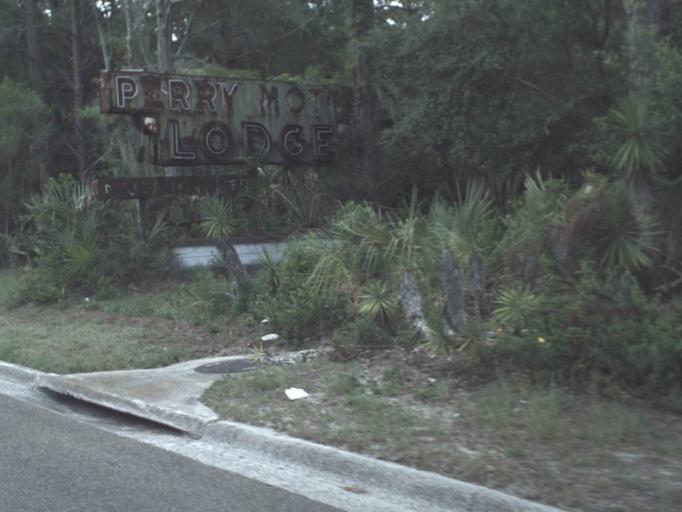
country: US
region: Florida
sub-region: Taylor County
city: Perry
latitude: 30.0799
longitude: -83.5658
